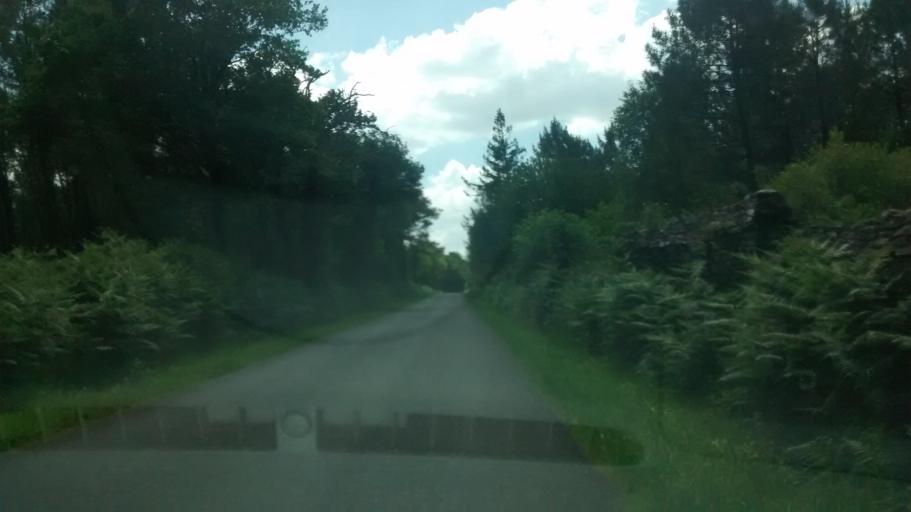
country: FR
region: Brittany
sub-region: Departement du Morbihan
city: Augan
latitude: 47.8814
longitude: -2.2443
